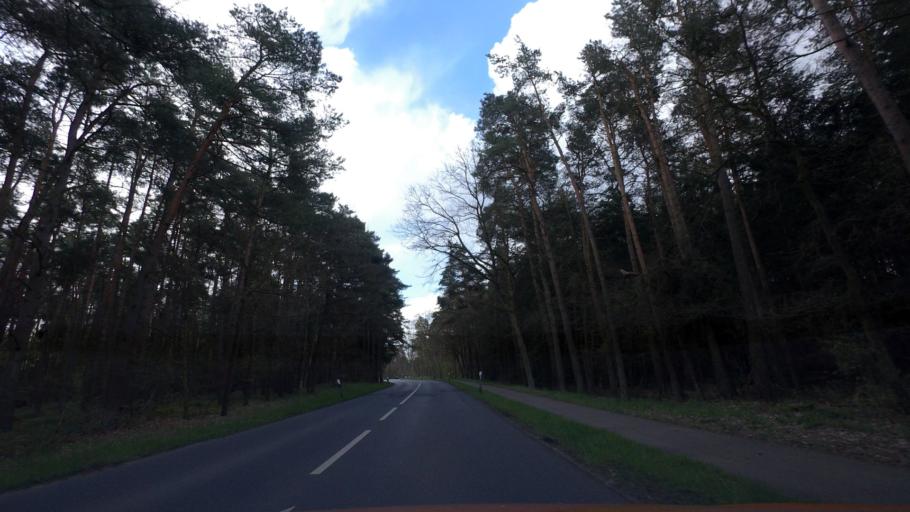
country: DE
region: Lower Saxony
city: Bardowick
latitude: 53.3013
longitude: 10.4107
